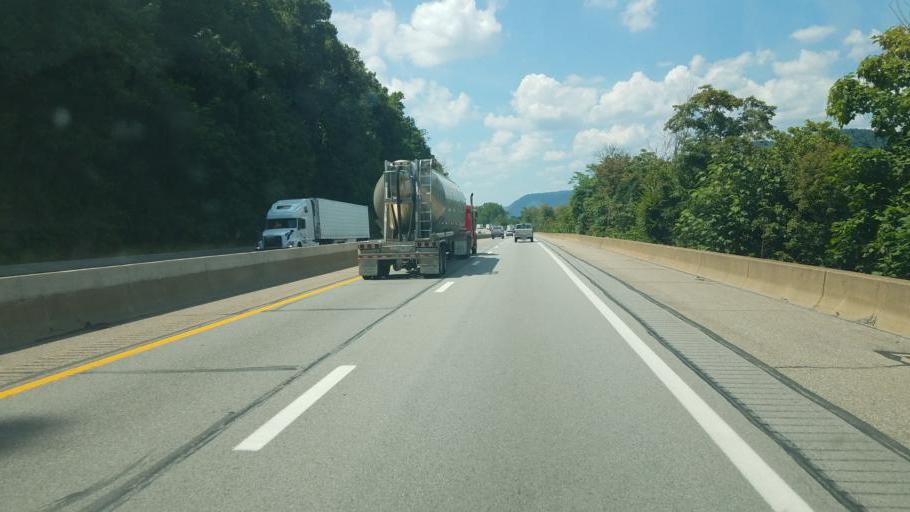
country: US
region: West Virginia
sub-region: Kanawha County
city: Chesapeake
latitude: 38.2033
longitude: -81.5157
